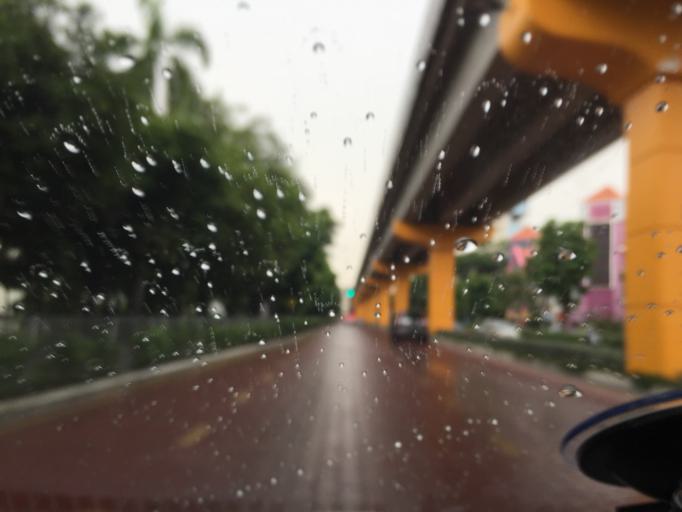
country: MY
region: Selangor
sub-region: Petaling
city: Petaling Jaya
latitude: 3.0735
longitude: 101.6108
